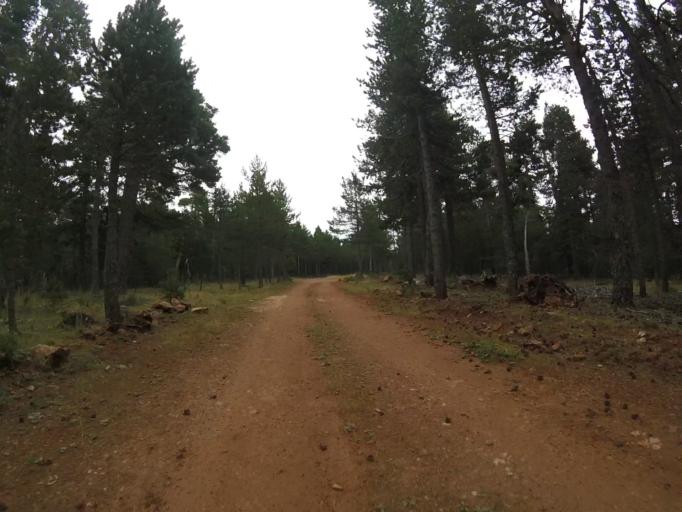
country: ES
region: Aragon
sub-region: Provincia de Teruel
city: Valdelinares
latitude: 40.3707
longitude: -0.6208
